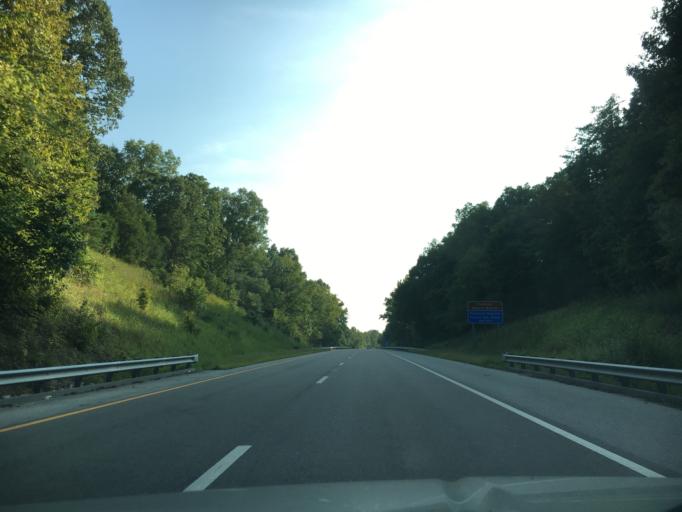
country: US
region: Virginia
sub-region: Prince Edward County
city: Farmville
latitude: 37.2736
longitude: -78.3697
